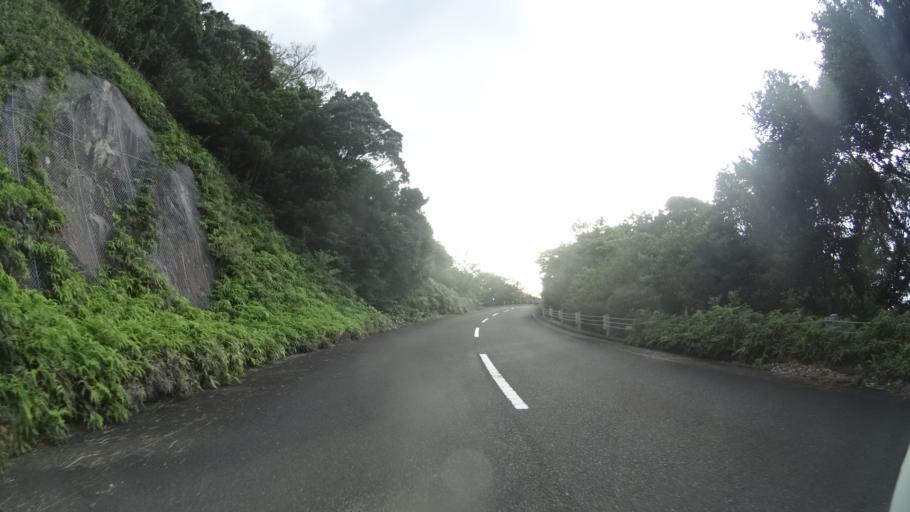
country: JP
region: Kagoshima
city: Nishinoomote
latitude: 30.3308
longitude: 130.3935
